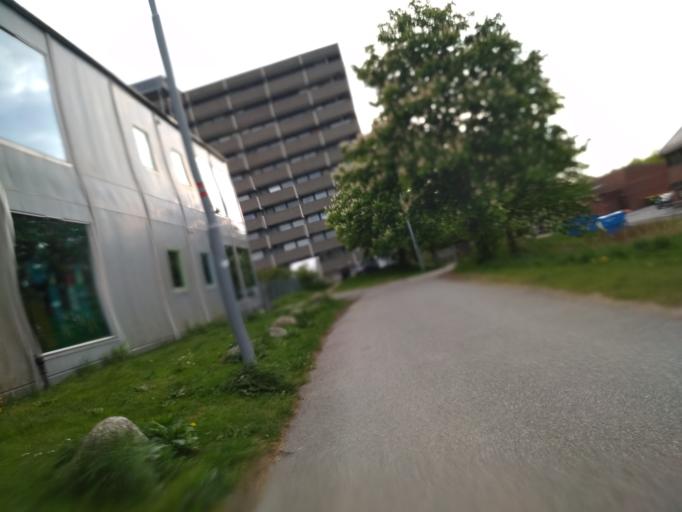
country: NO
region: Rogaland
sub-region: Stavanger
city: Stavanger
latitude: 58.9507
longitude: 5.7277
